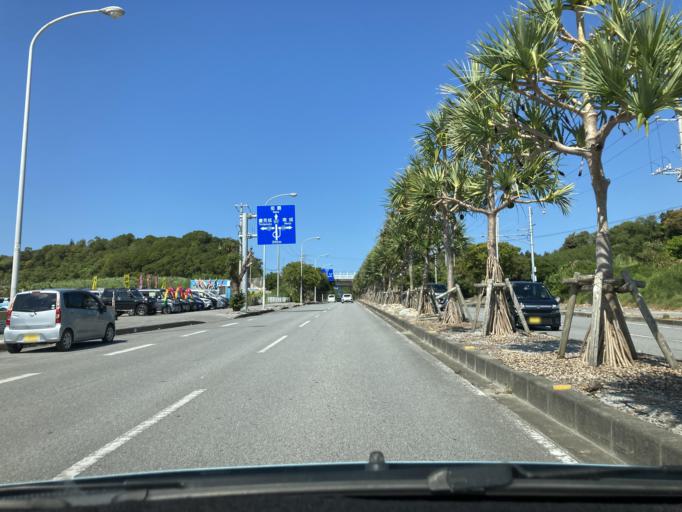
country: JP
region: Okinawa
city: Tomigusuku
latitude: 26.1822
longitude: 127.7235
